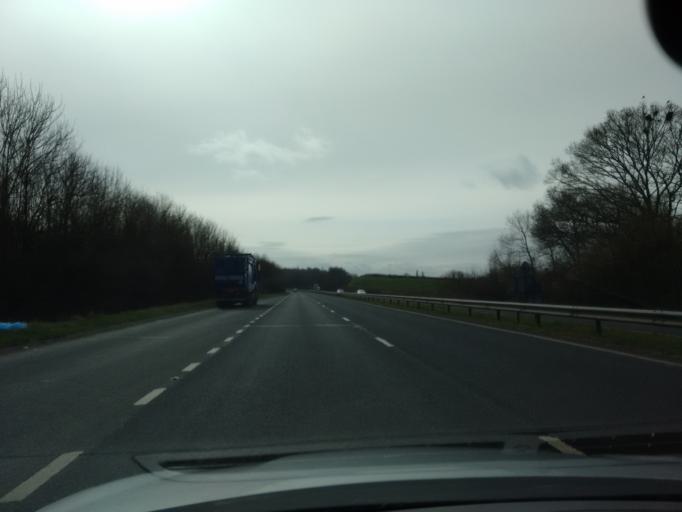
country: GB
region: England
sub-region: Warwickshire
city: Alcester
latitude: 52.2153
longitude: -1.8827
